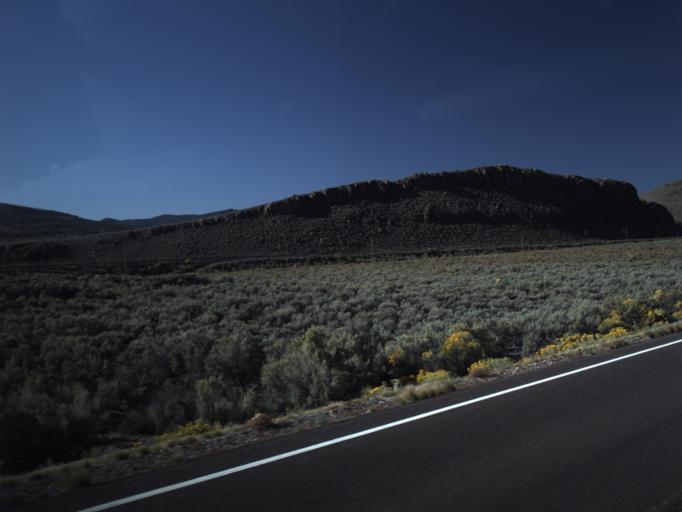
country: US
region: Utah
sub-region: Washington County
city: Enterprise
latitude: 37.7923
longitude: -113.9465
